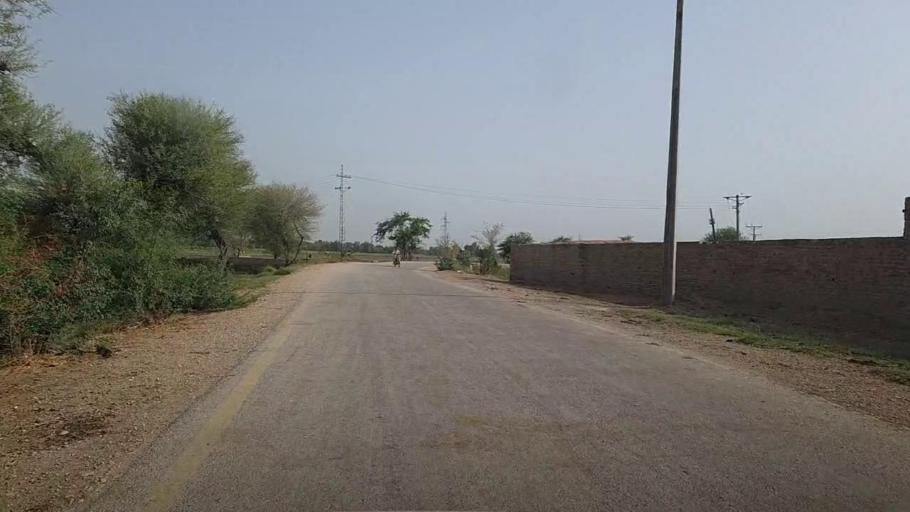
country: PK
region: Sindh
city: Khairpur Nathan Shah
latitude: 27.1039
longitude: 67.7572
